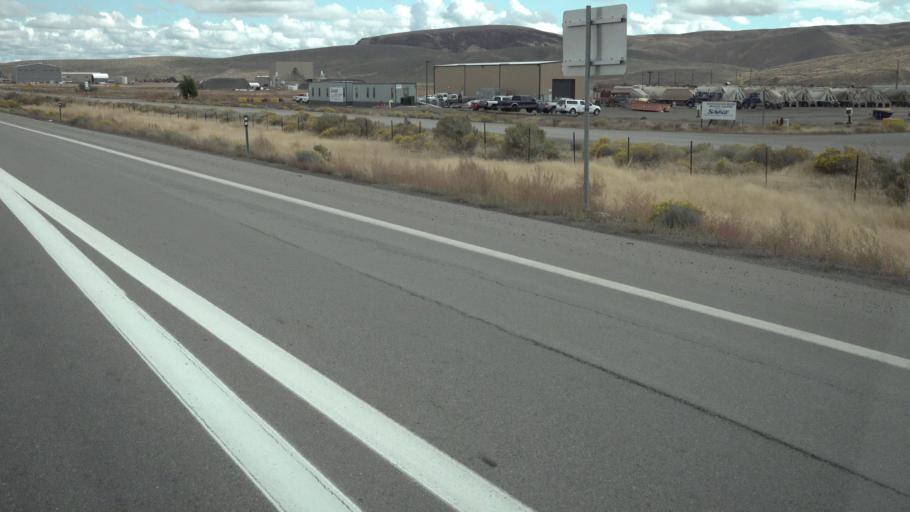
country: US
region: Nevada
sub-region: Elko County
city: Elko
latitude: 40.9358
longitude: -115.6612
